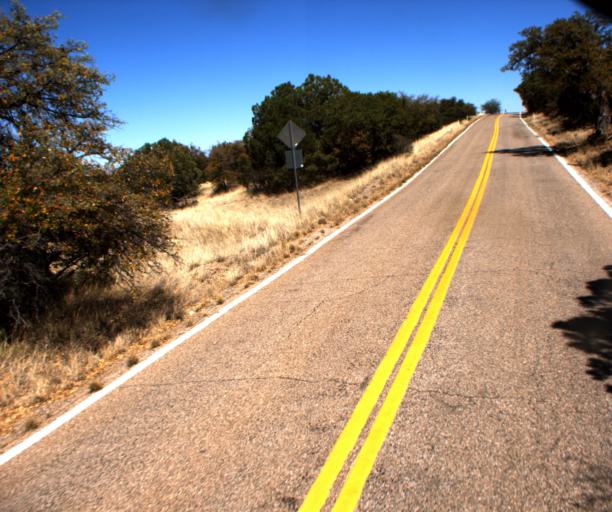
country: US
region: Arizona
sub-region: Cochise County
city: Huachuca City
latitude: 31.5519
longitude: -110.5457
